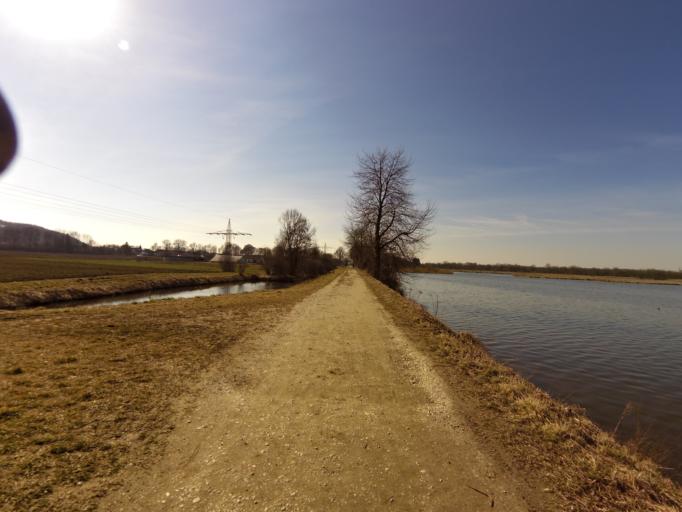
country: DE
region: Bavaria
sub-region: Lower Bavaria
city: Eching
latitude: 48.5011
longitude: 12.0449
